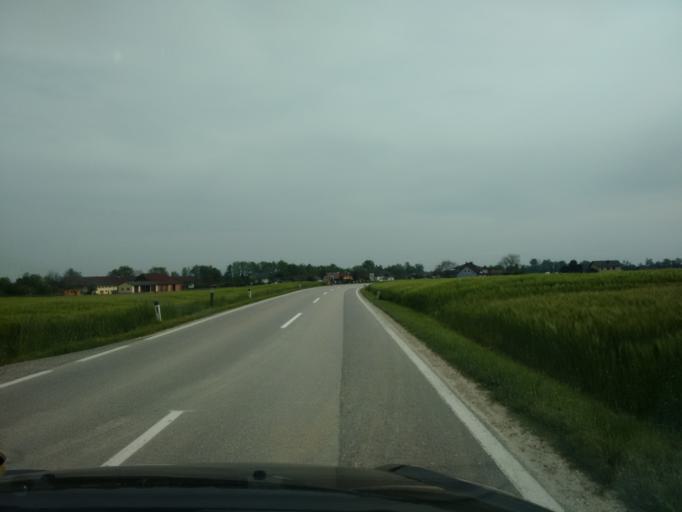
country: AT
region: Upper Austria
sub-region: Wels-Land
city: Marchtrenk
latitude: 48.1744
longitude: 14.1494
